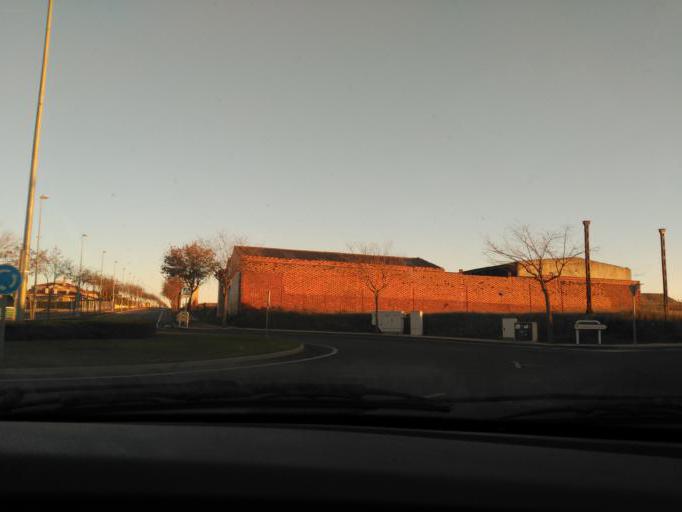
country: ES
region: Castille and Leon
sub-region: Provincia de Salamanca
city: Carbajosa de la Sagrada
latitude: 40.9387
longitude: -5.6398
